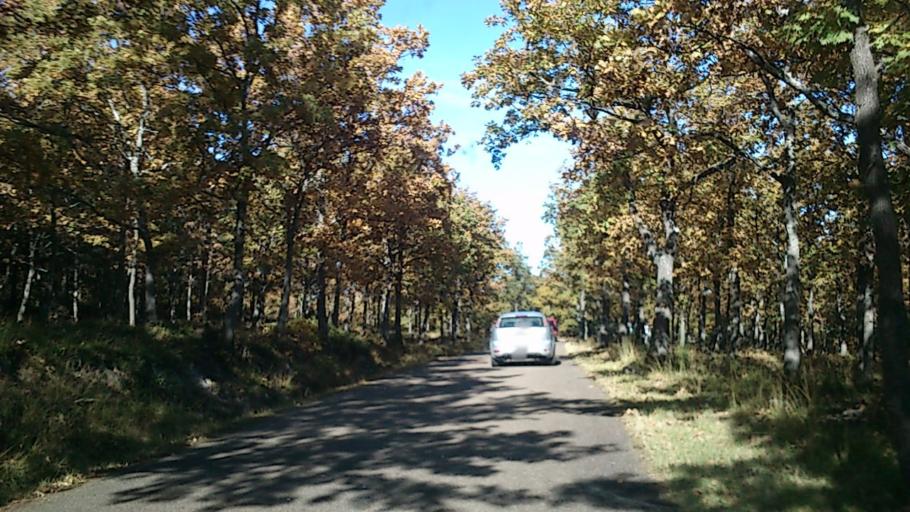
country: ES
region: Aragon
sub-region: Provincia de Zaragoza
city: Lituenigo
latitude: 41.8071
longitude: -1.8002
